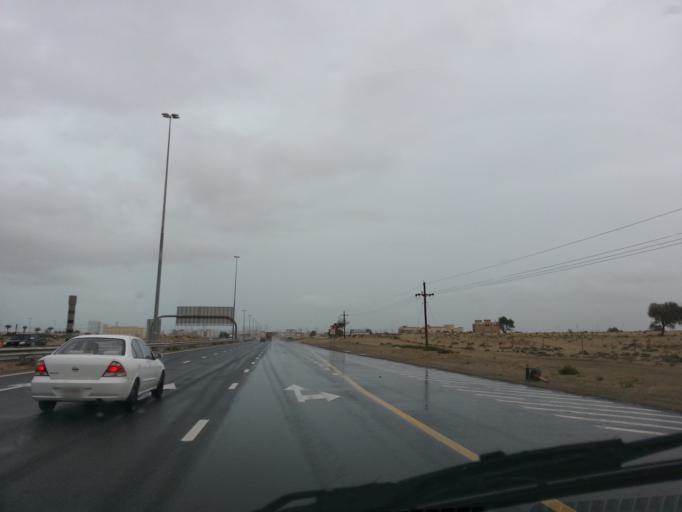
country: AE
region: Dubai
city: Dubai
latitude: 25.0598
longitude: 55.2217
